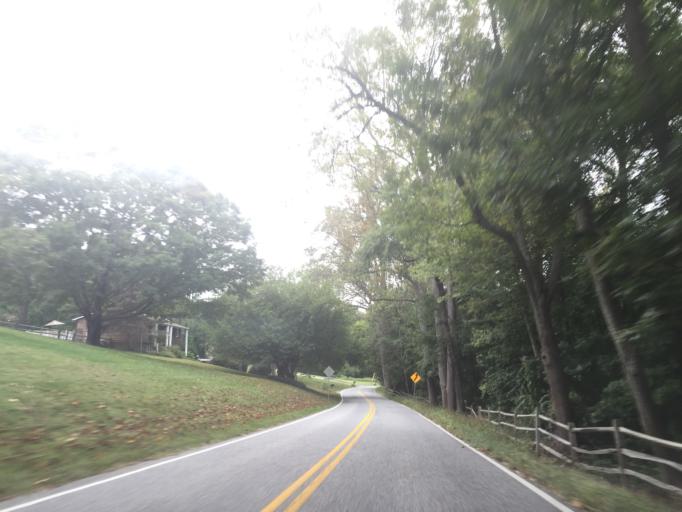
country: US
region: Maryland
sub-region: Harford County
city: Bel Air
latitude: 39.5018
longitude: -76.3630
